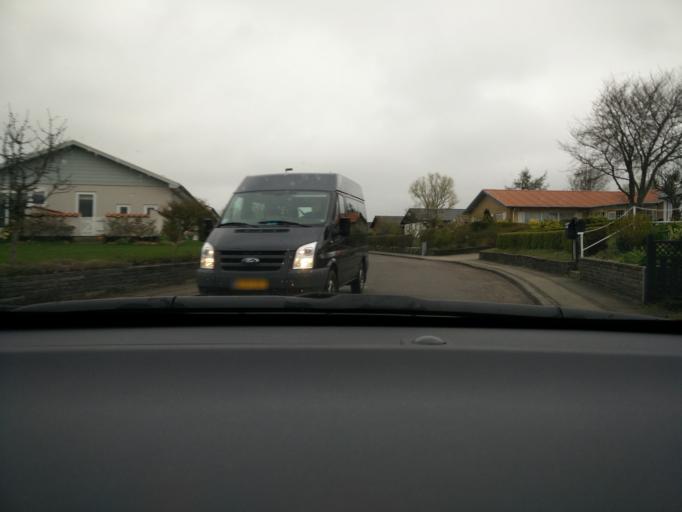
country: DK
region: Central Jutland
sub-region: Skive Kommune
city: Hojslev
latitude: 56.5458
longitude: 9.1233
